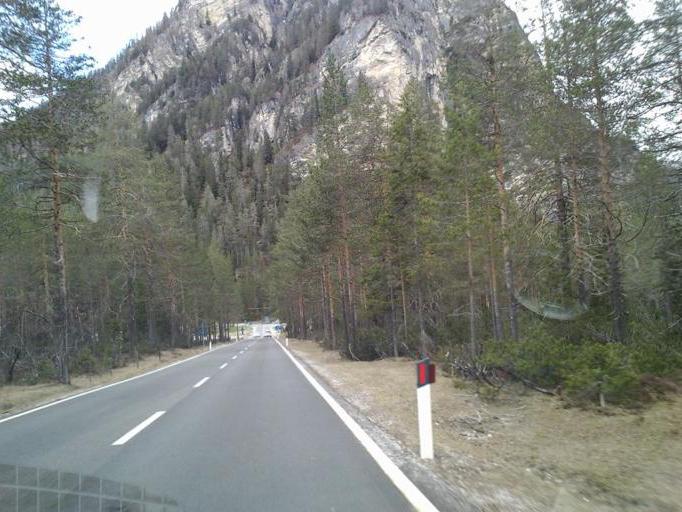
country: IT
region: Trentino-Alto Adige
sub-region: Bolzano
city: Dobbiaco
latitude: 46.6191
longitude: 12.2201
